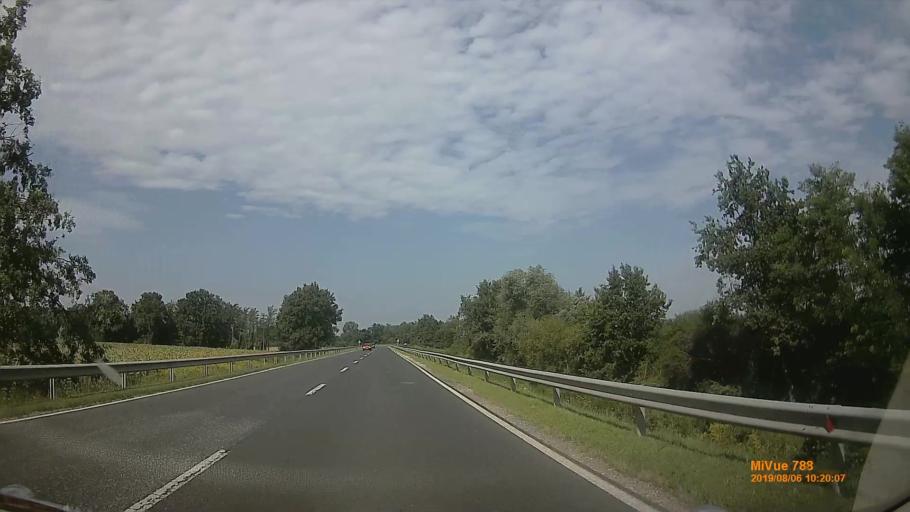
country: HU
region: Vas
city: Vasvar
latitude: 47.0590
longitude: 16.7617
